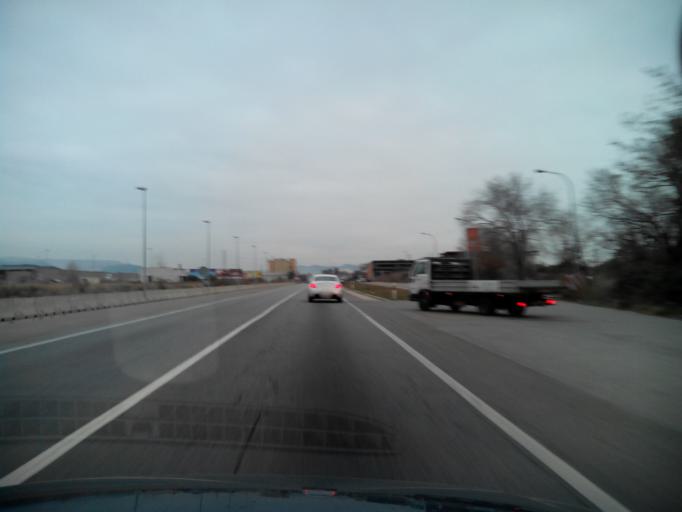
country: ES
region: Catalonia
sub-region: Provincia de Barcelona
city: Sant Fruitos de Bages
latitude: 41.7594
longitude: 1.8700
